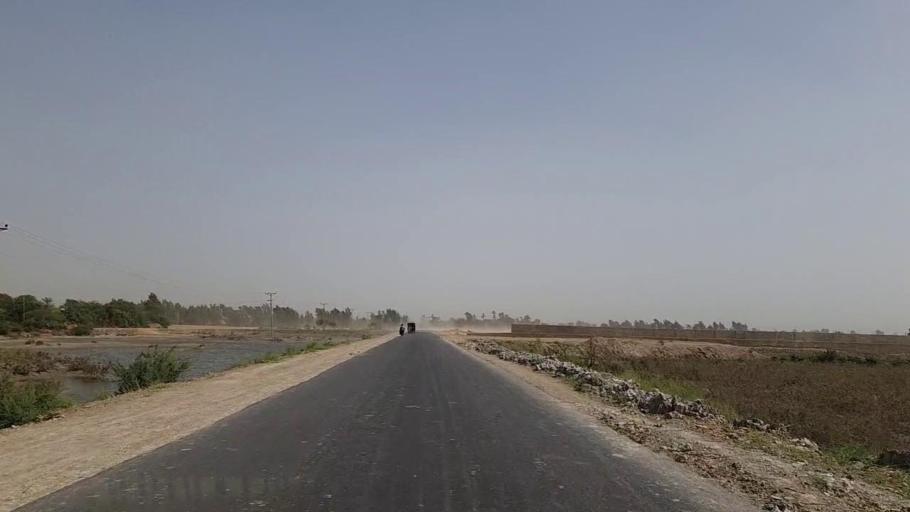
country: PK
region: Sindh
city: Tando Bago
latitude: 24.7959
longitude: 68.9496
